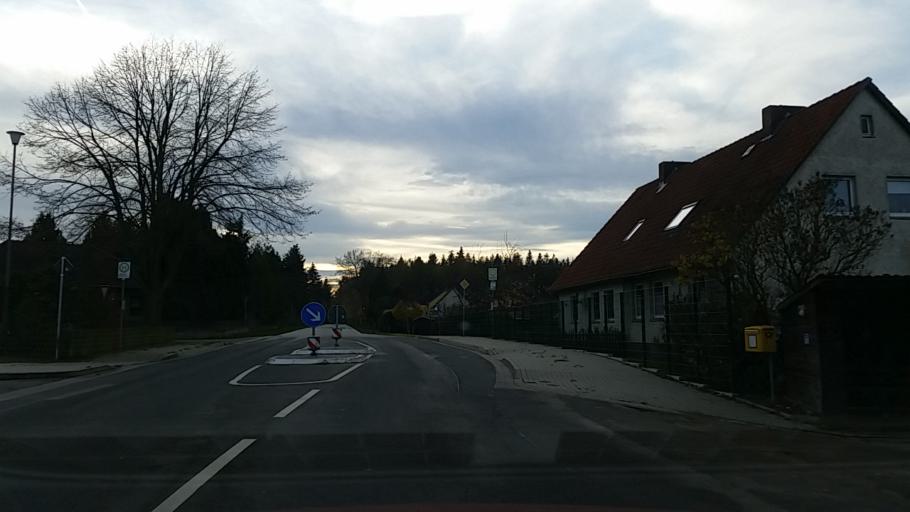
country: DE
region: Lower Saxony
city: Sprakensehl
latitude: 52.7899
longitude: 10.4989
